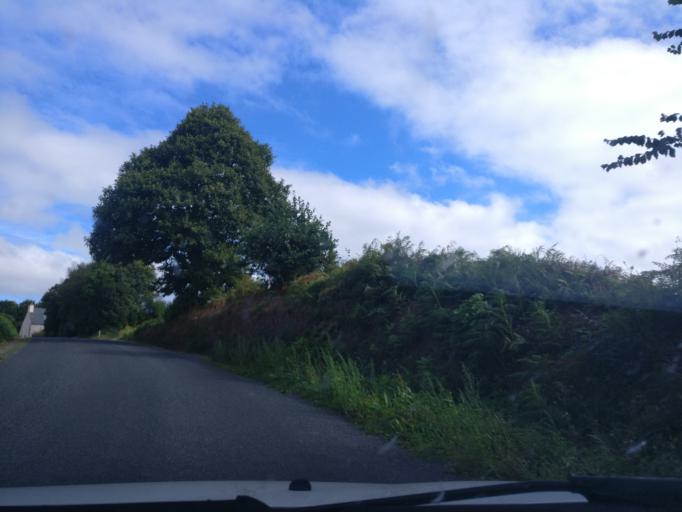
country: FR
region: Brittany
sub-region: Departement des Cotes-d'Armor
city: Rospez
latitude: 48.7403
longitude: -3.3736
